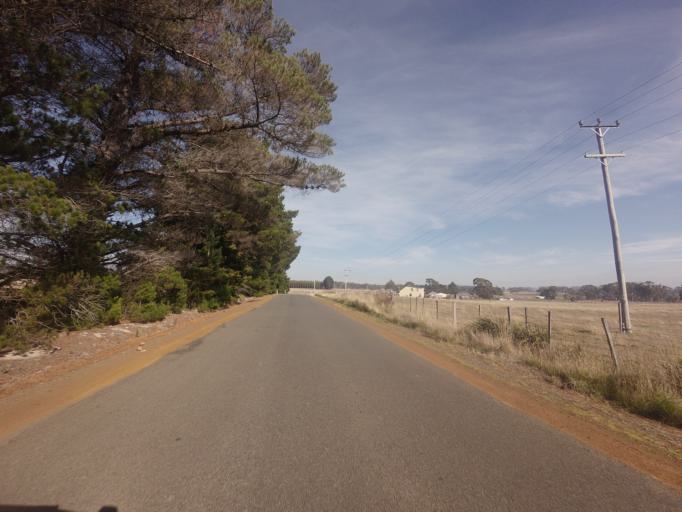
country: AU
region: Tasmania
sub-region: Sorell
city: Sorell
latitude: -42.4392
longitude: 147.4724
